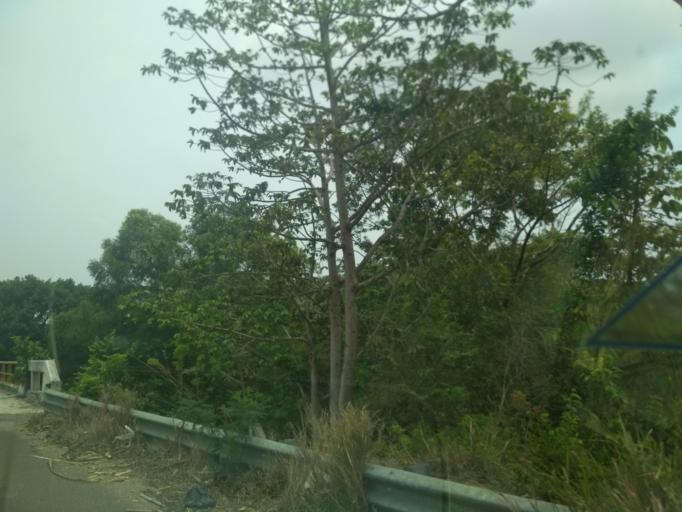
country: MX
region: Veracruz
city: Paso del Toro
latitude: 19.0373
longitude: -96.1525
